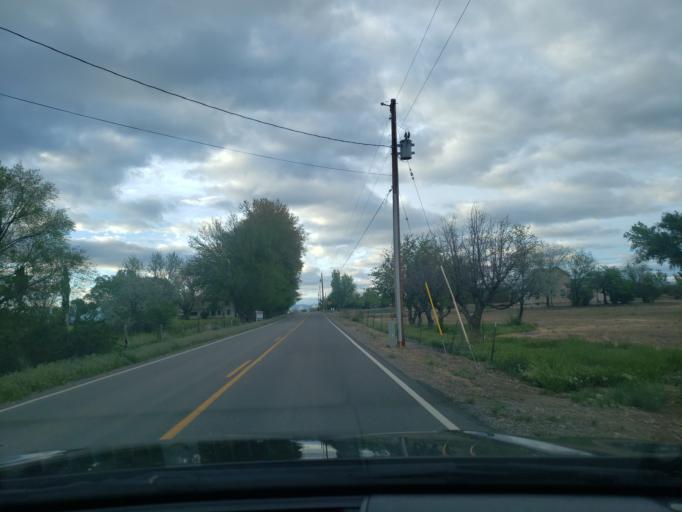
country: US
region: Colorado
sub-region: Mesa County
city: Fruita
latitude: 39.1799
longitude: -108.7290
